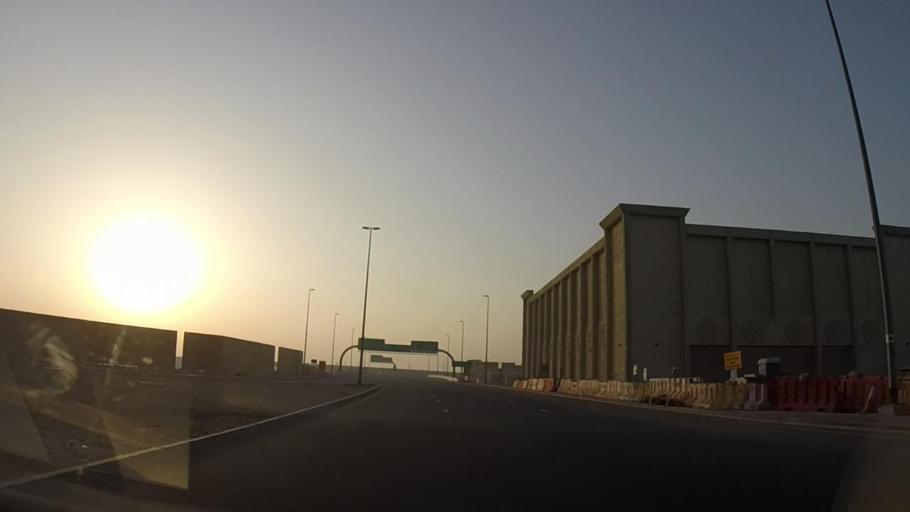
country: AE
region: Dubai
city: Dubai
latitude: 25.0613
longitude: 55.1378
